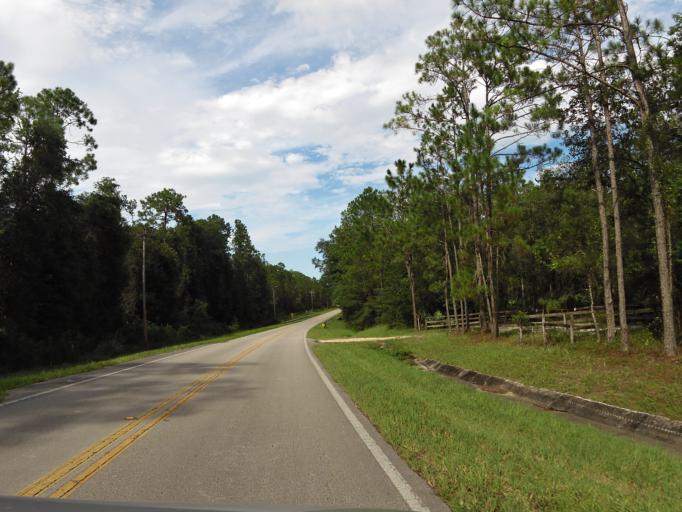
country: US
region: Florida
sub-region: Clay County
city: Green Cove Springs
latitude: 29.9253
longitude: -81.6797
